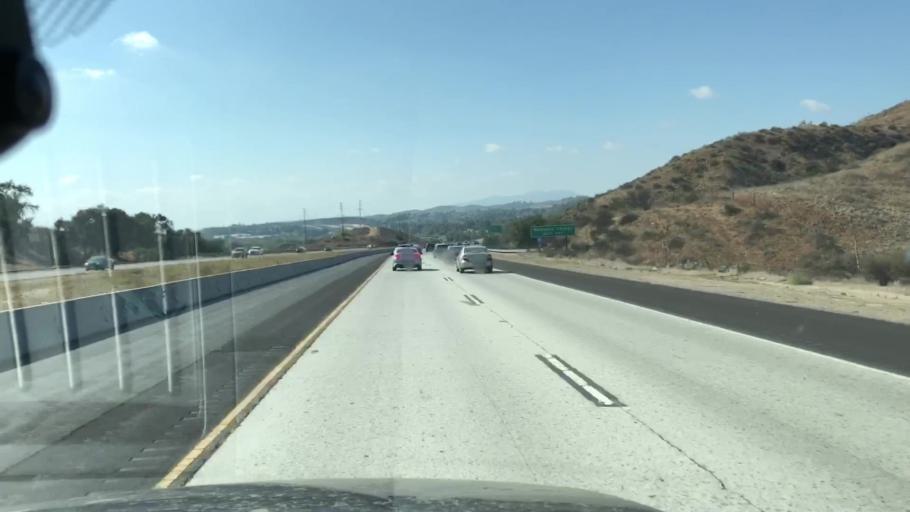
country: US
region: California
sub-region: Ventura County
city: Moorpark
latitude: 34.2923
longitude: -118.8294
